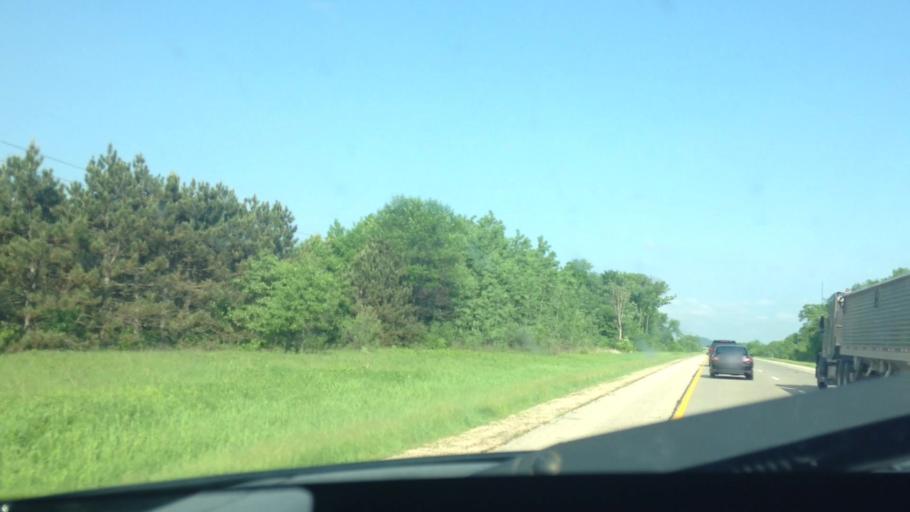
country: US
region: Wisconsin
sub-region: Juneau County
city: New Lisbon
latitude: 43.8985
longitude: -90.1847
